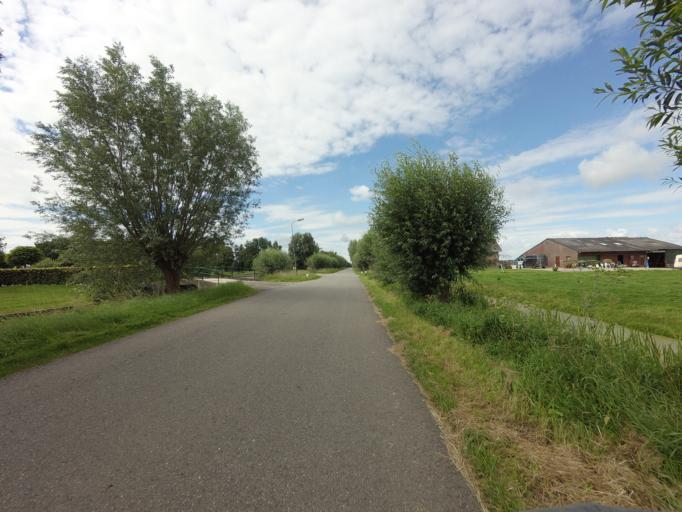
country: NL
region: Utrecht
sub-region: Gemeente Oudewater
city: Oudewater
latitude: 52.0066
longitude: 4.8593
